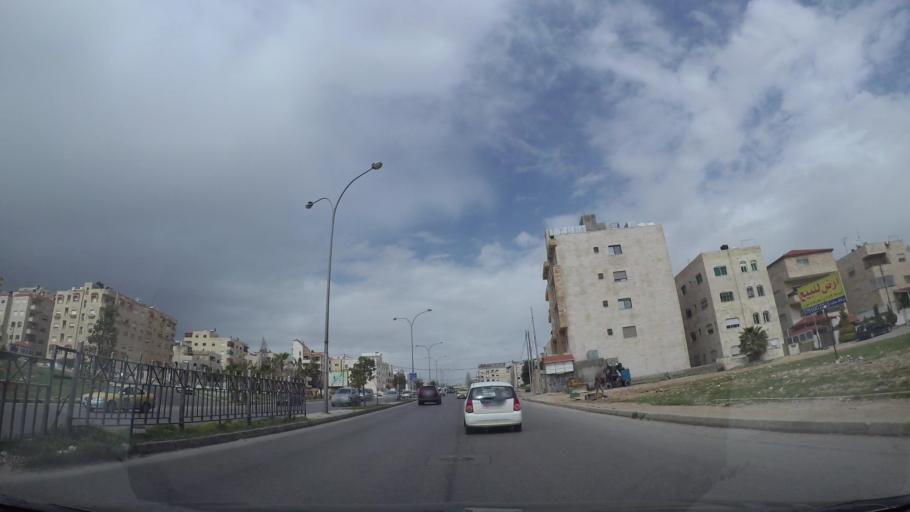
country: JO
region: Amman
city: Amman
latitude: 31.9851
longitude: 35.9180
